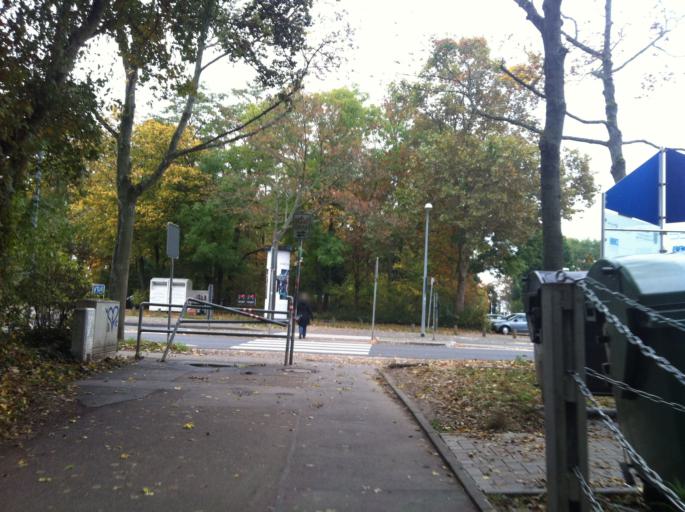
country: DE
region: Rheinland-Pfalz
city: Mainz
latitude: 49.9842
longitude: 8.2915
